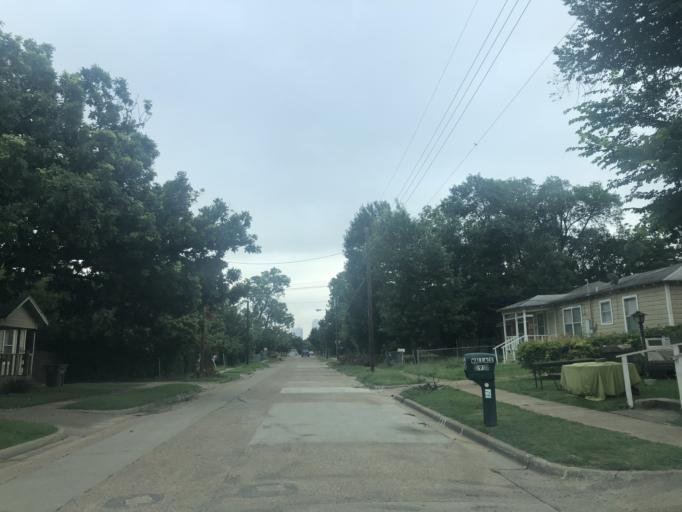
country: US
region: Texas
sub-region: Dallas County
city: Dallas
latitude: 32.7810
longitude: -96.8513
